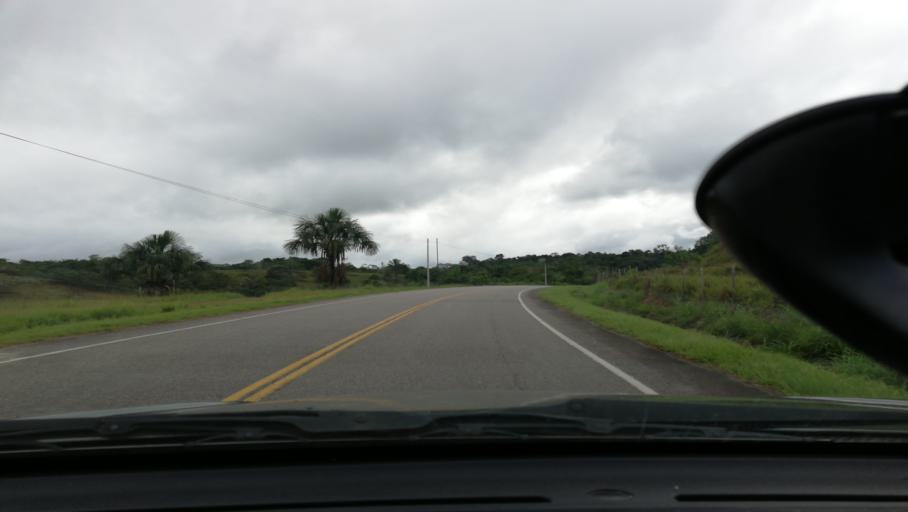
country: PE
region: Loreto
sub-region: Provincia de Loreto
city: Nauta
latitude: -4.4862
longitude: -73.5991
